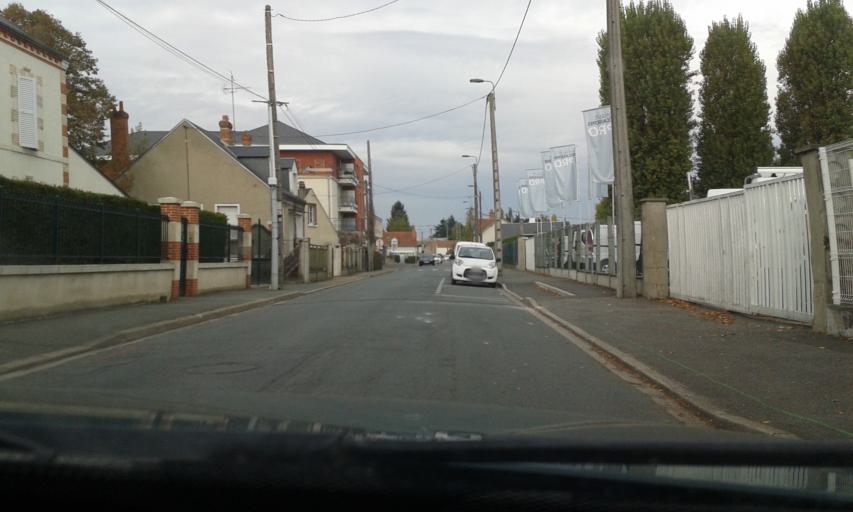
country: FR
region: Centre
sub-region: Departement du Loiret
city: Saran
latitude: 47.9360
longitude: 1.8924
